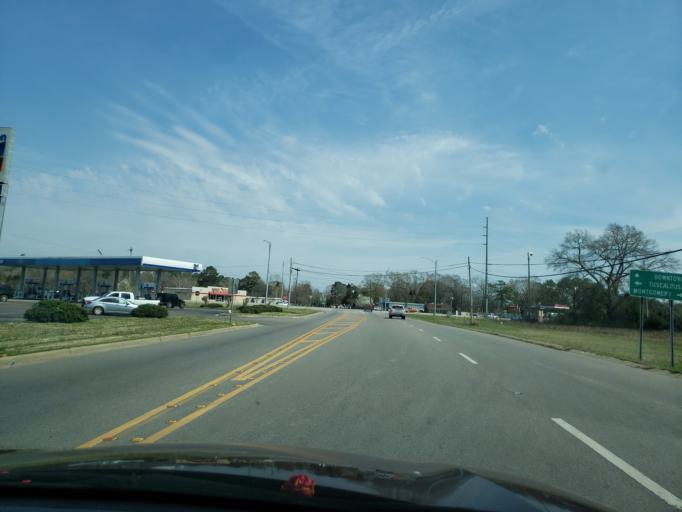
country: US
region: Alabama
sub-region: Autauga County
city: Prattville
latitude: 32.4376
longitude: -86.4749
